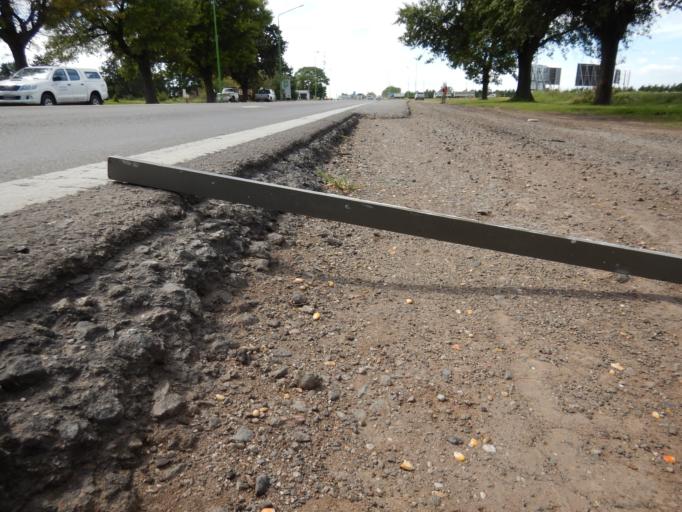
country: AR
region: Santa Fe
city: Carcarana
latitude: -32.8669
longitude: -61.1259
